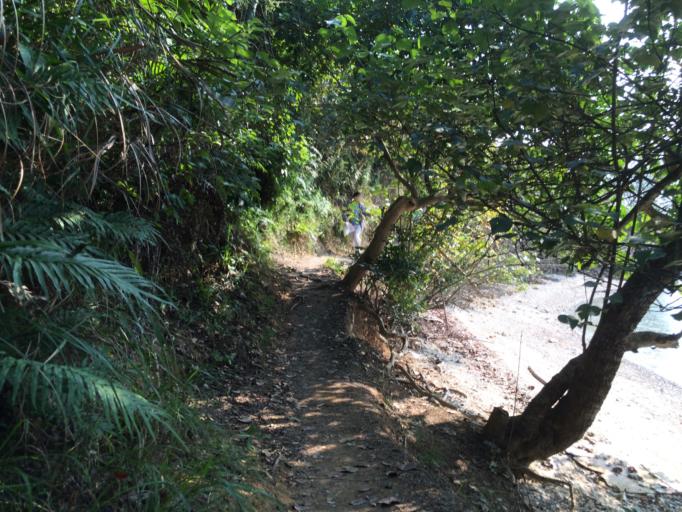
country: HK
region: Tai Po
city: Tai Po
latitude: 22.4492
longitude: 114.2249
